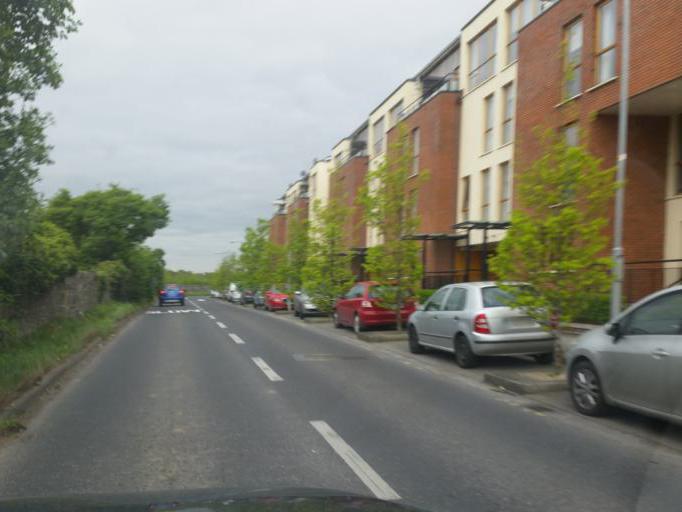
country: IE
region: Leinster
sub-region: Dublin City
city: Finglas
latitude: 53.3782
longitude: -6.3287
